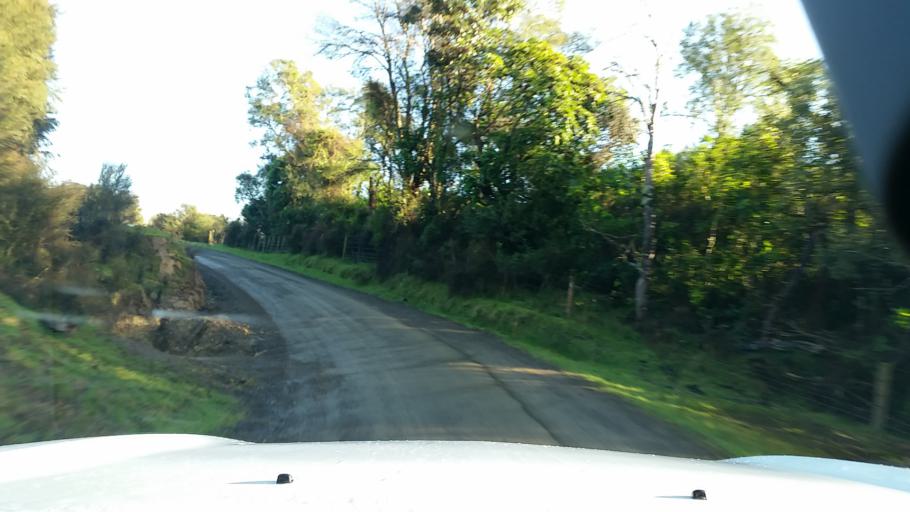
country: NZ
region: Wellington
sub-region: South Wairarapa District
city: Waipawa
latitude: -41.3232
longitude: 175.6559
